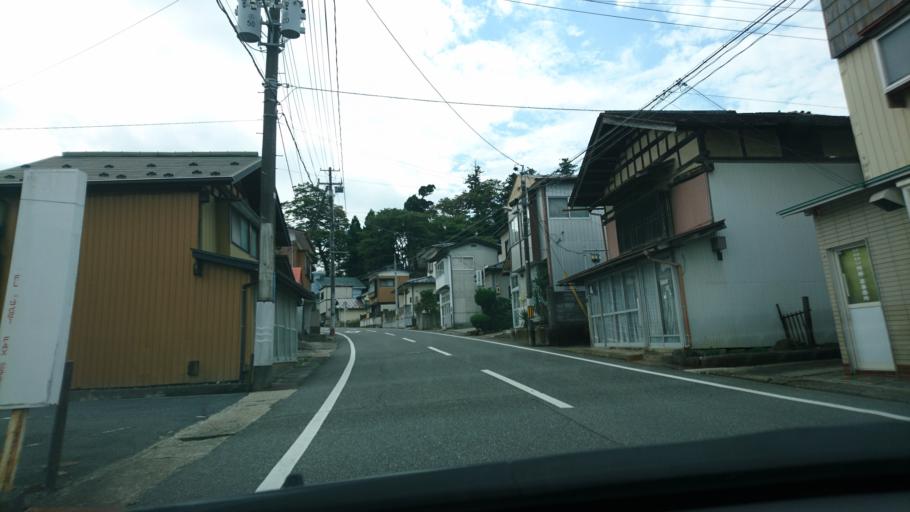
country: JP
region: Miyagi
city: Furukawa
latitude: 38.7320
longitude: 141.0186
